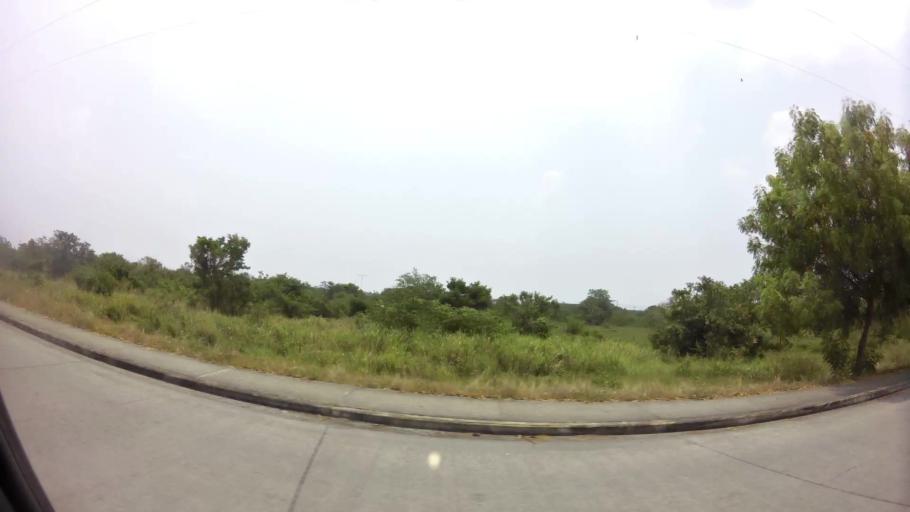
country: HN
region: Cortes
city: La Lima
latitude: 15.4501
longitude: -87.9362
